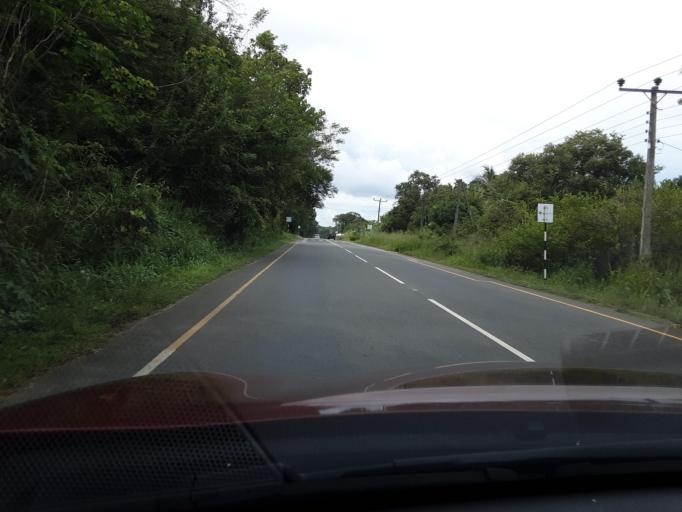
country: LK
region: Uva
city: Badulla
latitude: 7.3937
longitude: 81.1292
